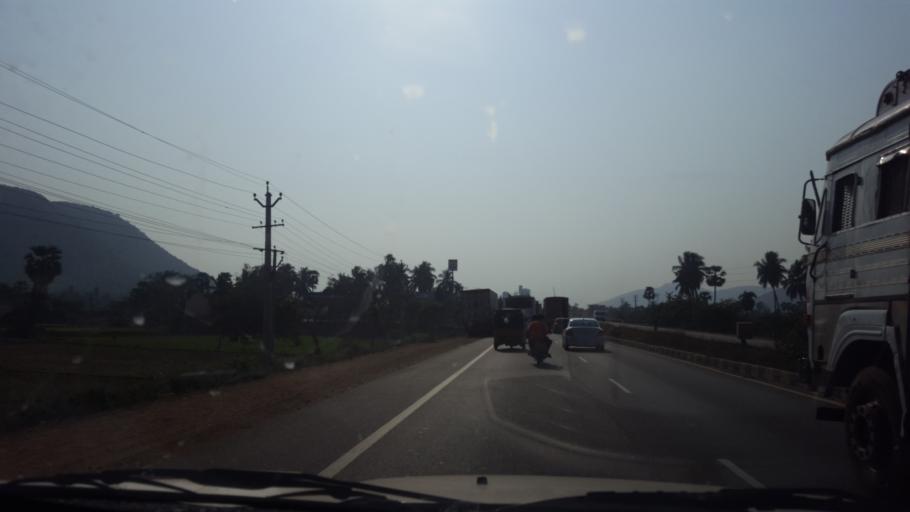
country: IN
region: Andhra Pradesh
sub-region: Vishakhapatnam
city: Anakapalle
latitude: 17.6609
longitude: 82.9406
